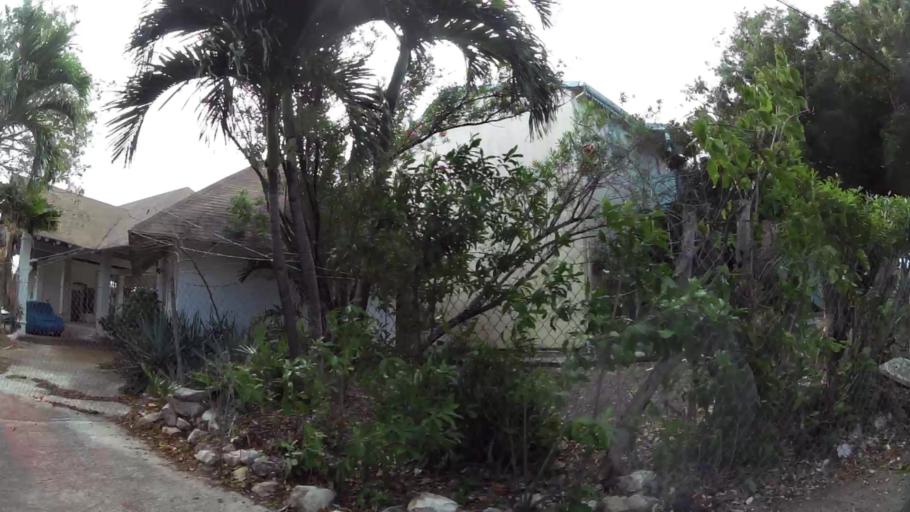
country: AG
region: Saint Peter
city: Parham
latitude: 17.1008
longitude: -61.6849
